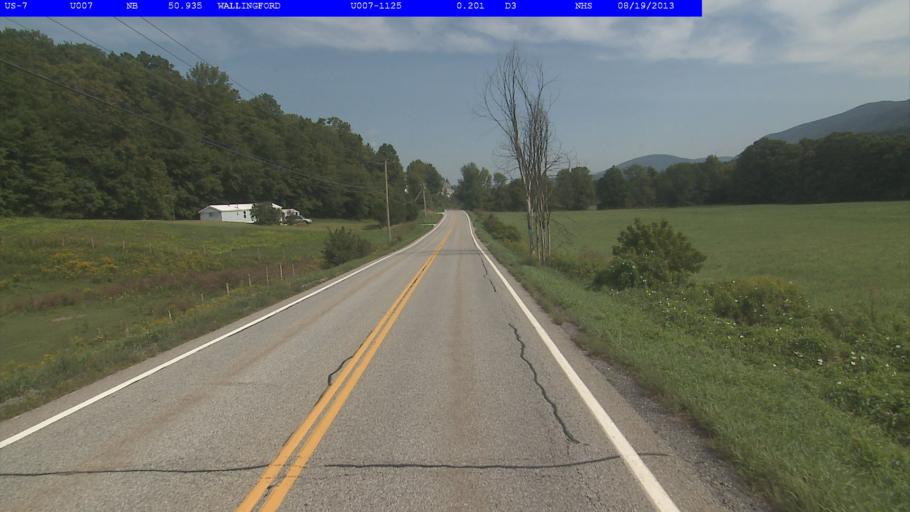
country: US
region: Vermont
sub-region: Rutland County
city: West Rutland
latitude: 43.4003
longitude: -72.9984
